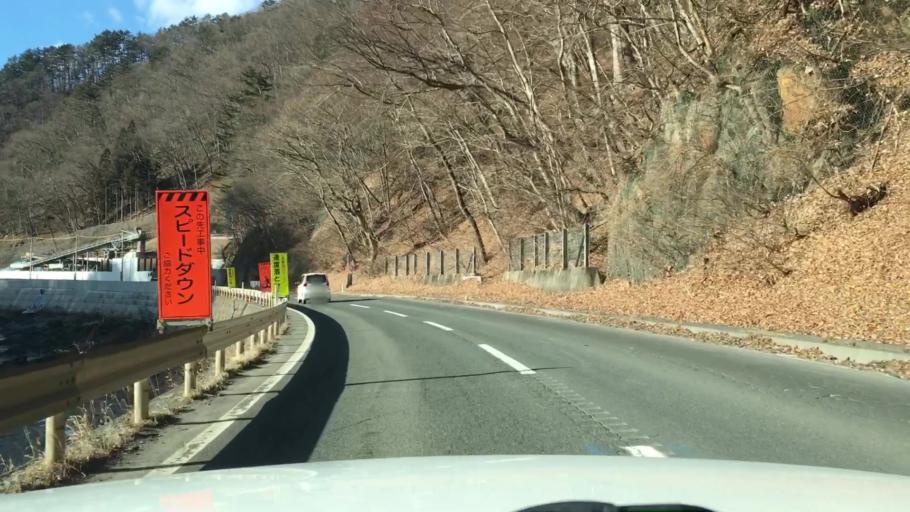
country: JP
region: Iwate
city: Miyako
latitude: 39.6005
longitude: 141.7125
